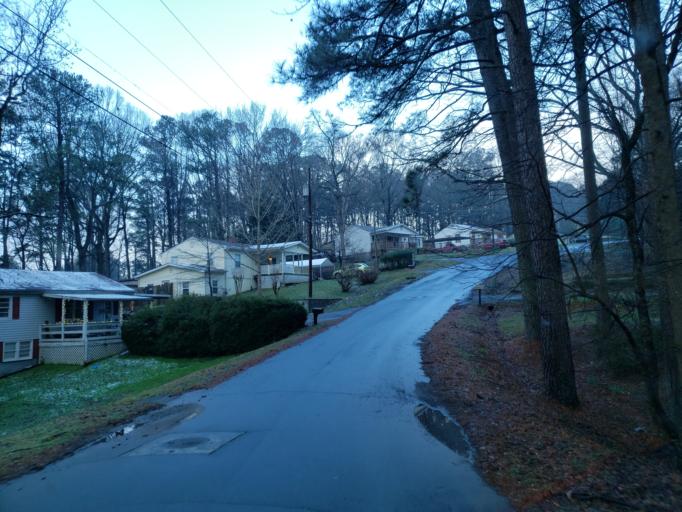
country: US
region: Georgia
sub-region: Cobb County
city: Kennesaw
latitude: 34.0297
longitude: -84.6134
